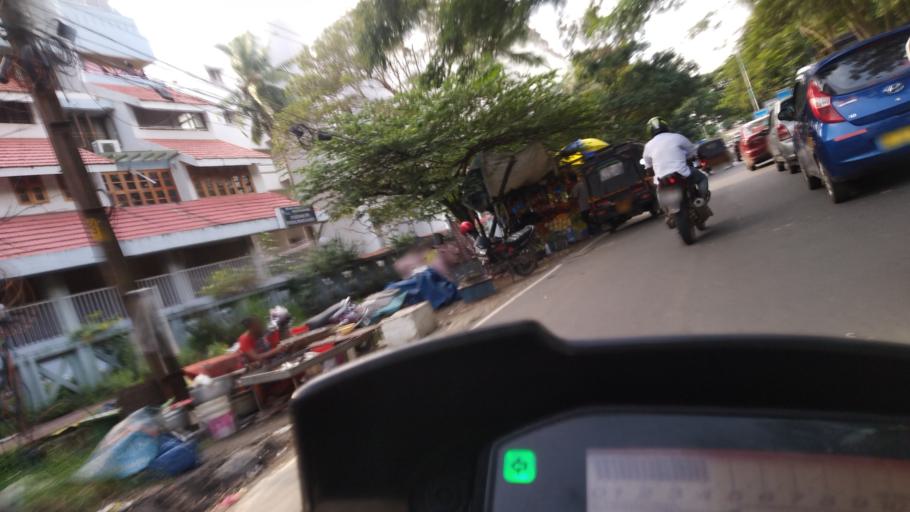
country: IN
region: Kerala
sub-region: Ernakulam
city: Cochin
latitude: 9.9852
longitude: 76.2732
